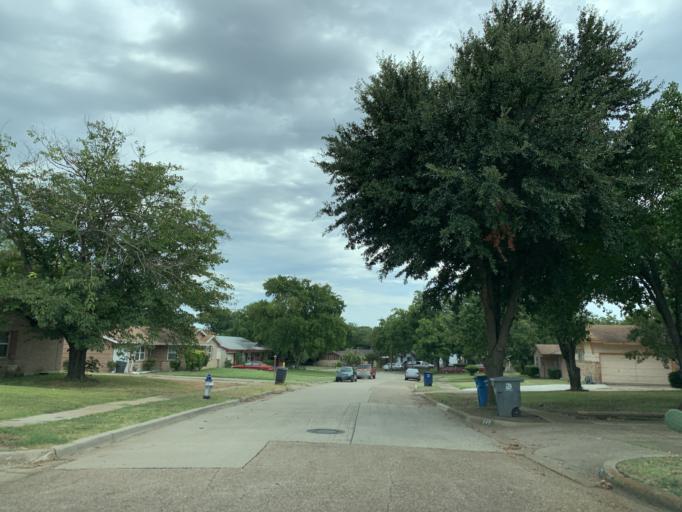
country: US
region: Texas
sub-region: Dallas County
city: DeSoto
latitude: 32.6571
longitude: -96.8291
